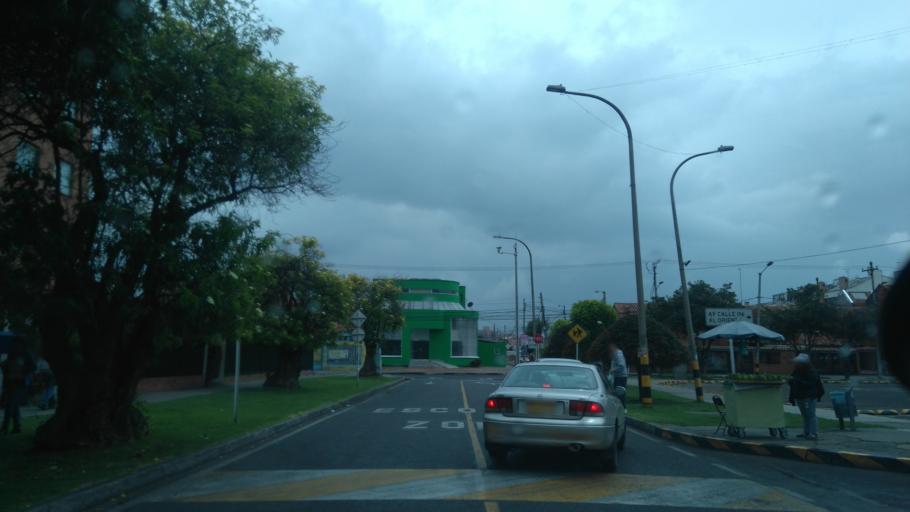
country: CO
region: Bogota D.C.
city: Barrio San Luis
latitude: 4.6985
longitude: -74.0574
